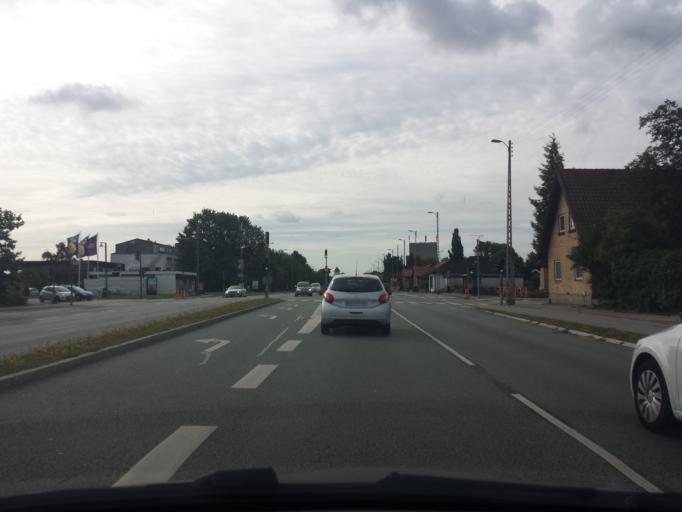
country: DK
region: Capital Region
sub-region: Rodovre Kommune
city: Rodovre
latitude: 55.6862
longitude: 12.4507
